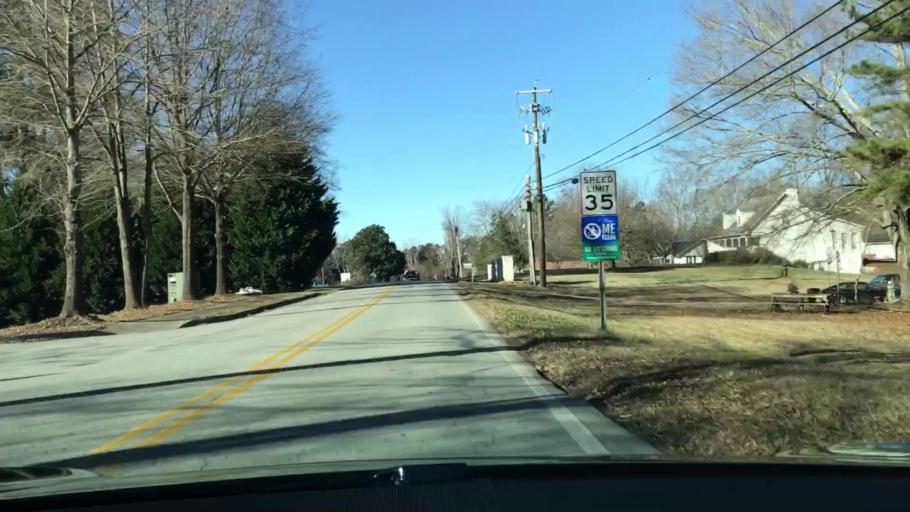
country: US
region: Georgia
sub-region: Gwinnett County
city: Buford
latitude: 34.1427
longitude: -84.0098
